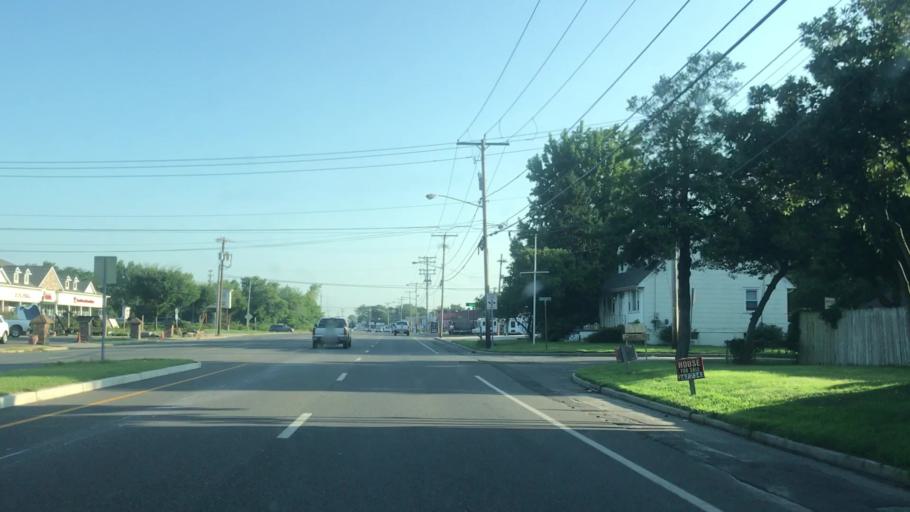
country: US
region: New Jersey
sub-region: Ocean County
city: Ocean Gate
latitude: 39.9519
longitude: -74.1240
